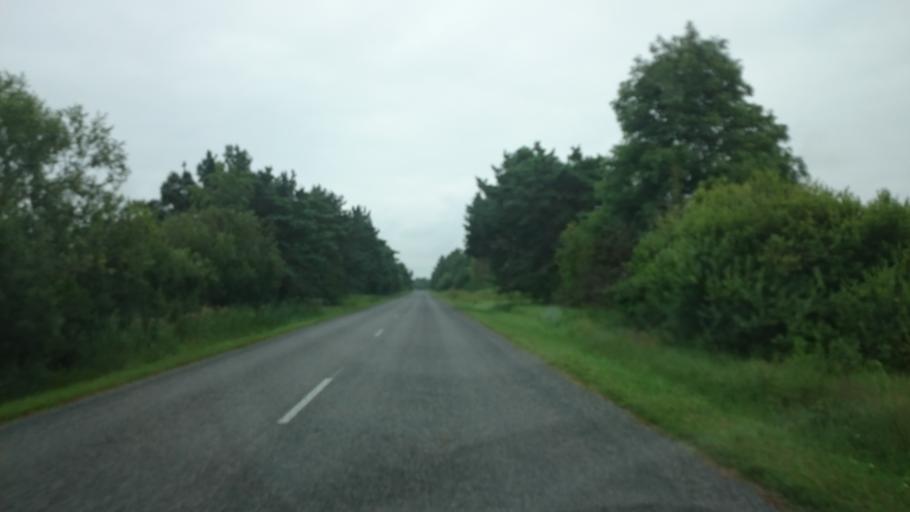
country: EE
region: Saare
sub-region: Orissaare vald
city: Orissaare
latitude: 58.5799
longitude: 23.0276
